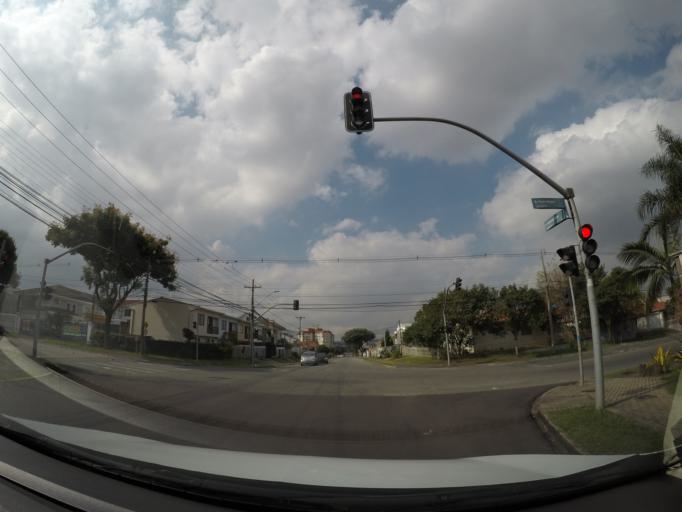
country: BR
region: Parana
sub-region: Curitiba
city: Curitiba
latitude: -25.4872
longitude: -49.2572
